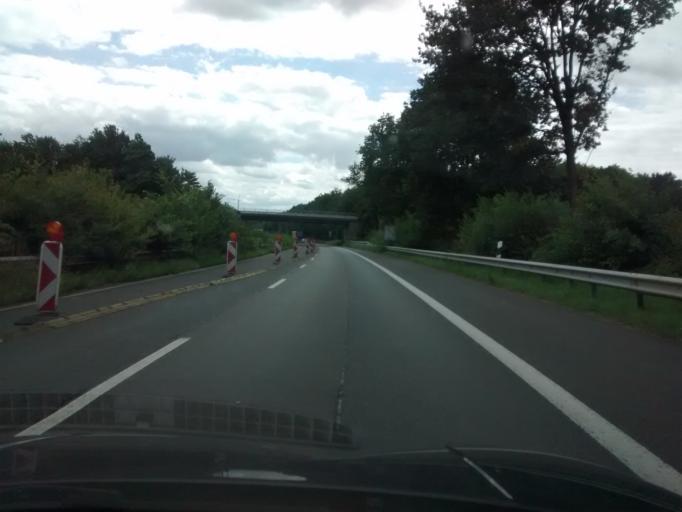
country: DE
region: Lower Saxony
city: Cloppenburg
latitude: 52.8524
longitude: 8.0274
